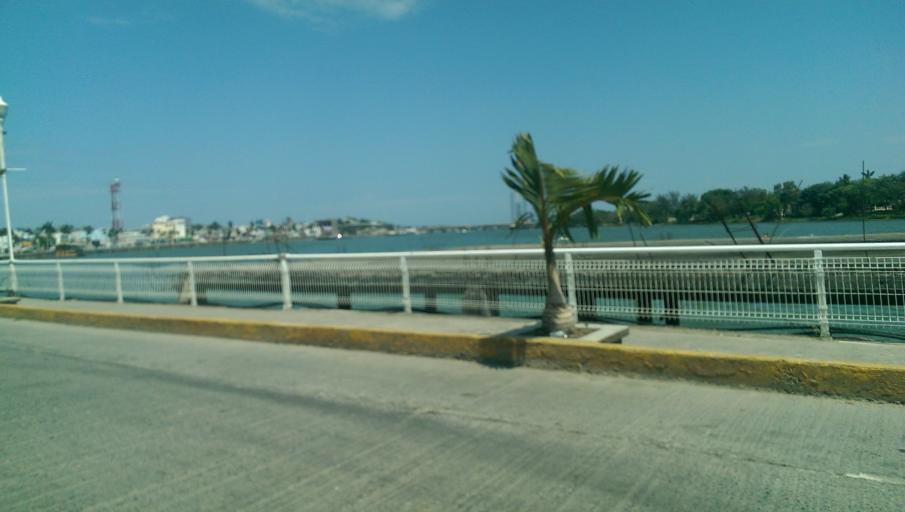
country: MX
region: Veracruz
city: Tuxpan de Rodriguez Cano
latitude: 20.9519
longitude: -97.4138
